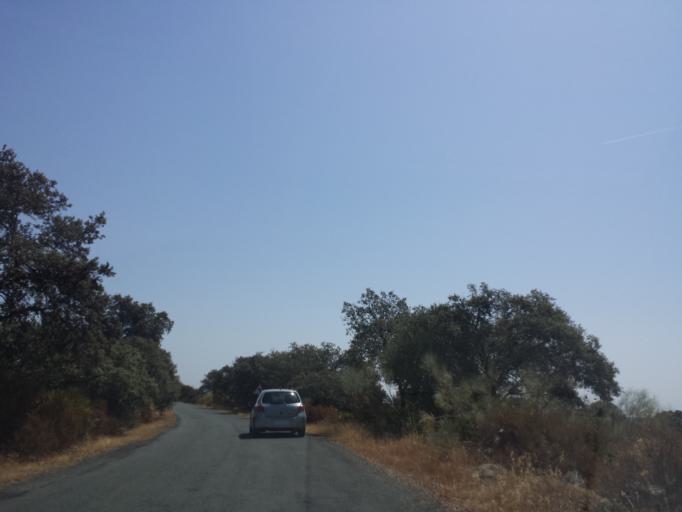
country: ES
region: Andalusia
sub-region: Provincia de Sevilla
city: Castilblanco de los Arroyos
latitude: 37.6828
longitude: -5.9668
